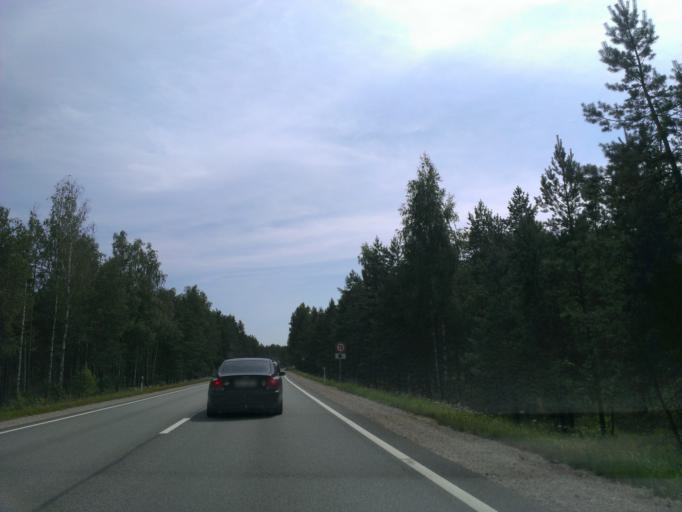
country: LV
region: Riga
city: Bergi
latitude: 56.9622
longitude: 24.3724
